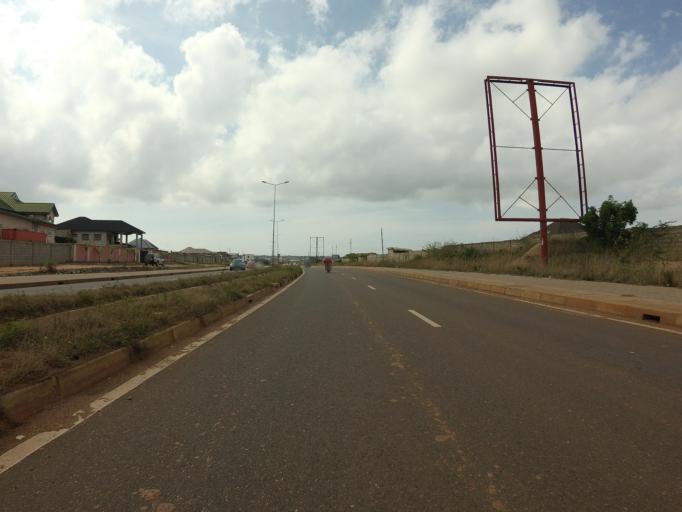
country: GH
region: Greater Accra
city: Teshi Old Town
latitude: 5.6012
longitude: -0.1371
